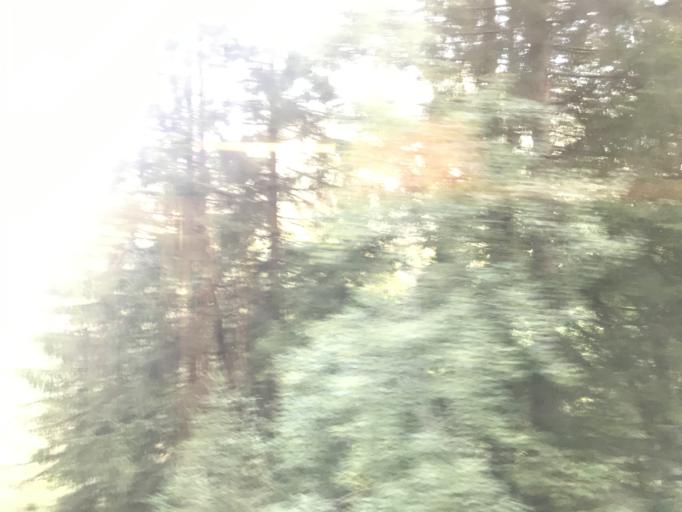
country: DE
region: Bavaria
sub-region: Upper Bavaria
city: Garmisch-Partenkirchen
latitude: 47.4754
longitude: 11.0654
